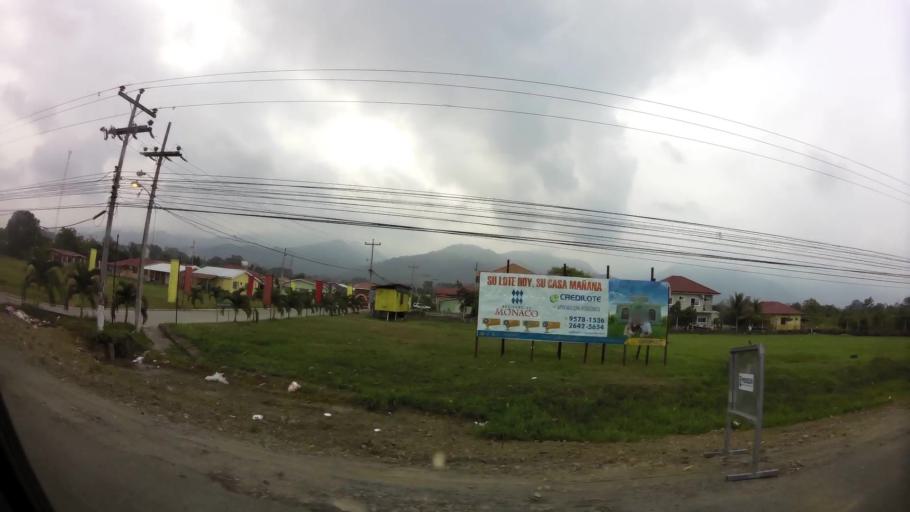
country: HN
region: Yoro
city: El Progreso
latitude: 15.4444
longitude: -87.7908
